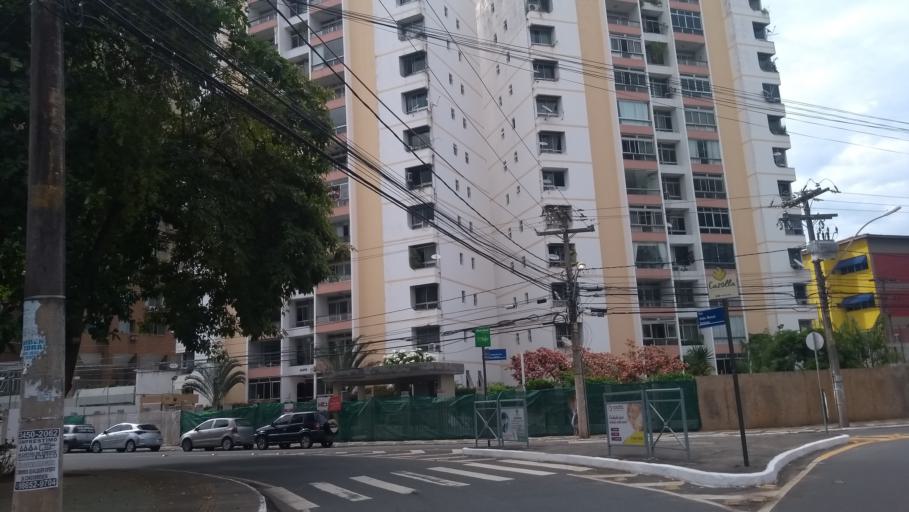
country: BR
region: Bahia
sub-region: Salvador
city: Salvador
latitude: -12.9931
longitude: -38.4627
